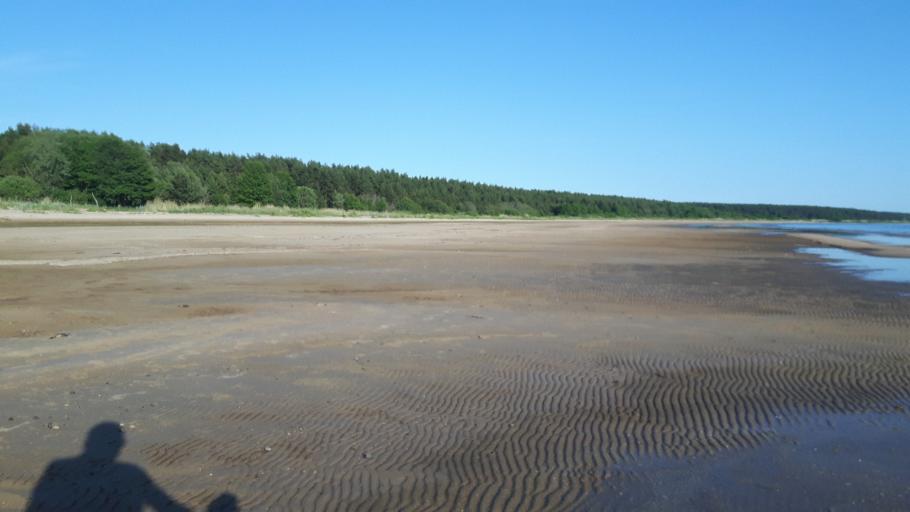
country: LV
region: Salacgrivas
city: Salacgriva
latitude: 57.6942
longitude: 24.3494
